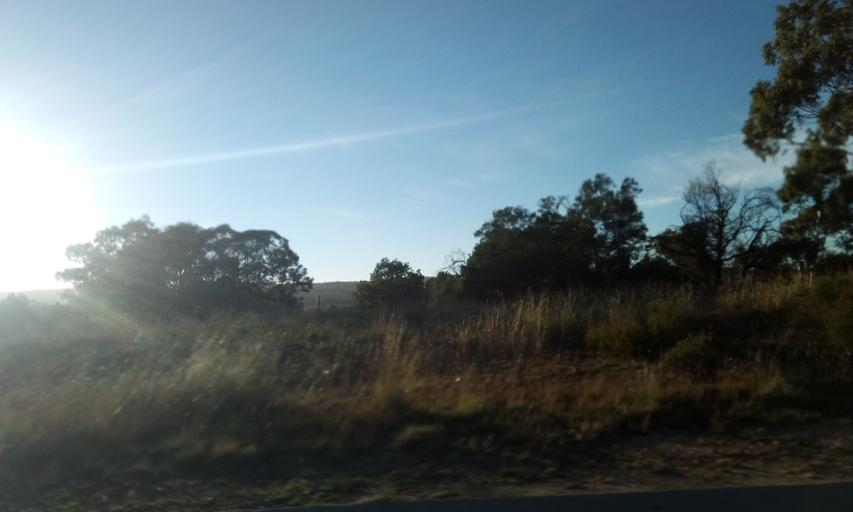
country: AU
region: New South Wales
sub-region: Yass Valley
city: Gundaroo
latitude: -35.1297
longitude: 149.3417
